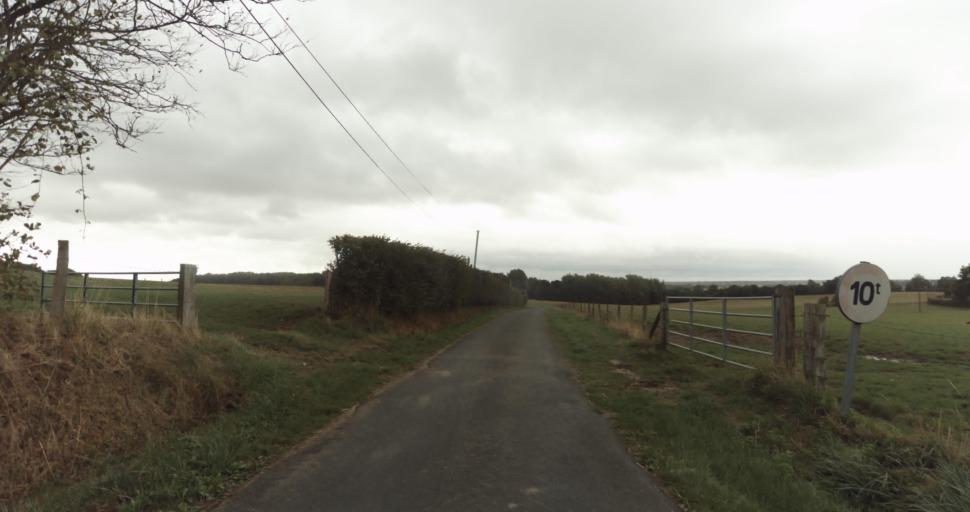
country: FR
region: Lower Normandy
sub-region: Departement de l'Orne
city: Sainte-Gauburge-Sainte-Colombe
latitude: 48.7418
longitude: 0.4718
